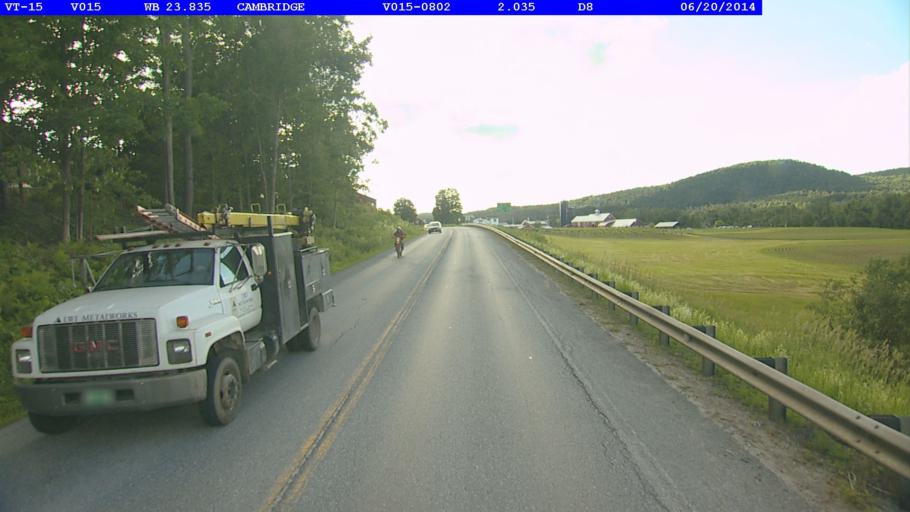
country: US
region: Vermont
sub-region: Chittenden County
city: Jericho
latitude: 44.6464
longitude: -72.8850
